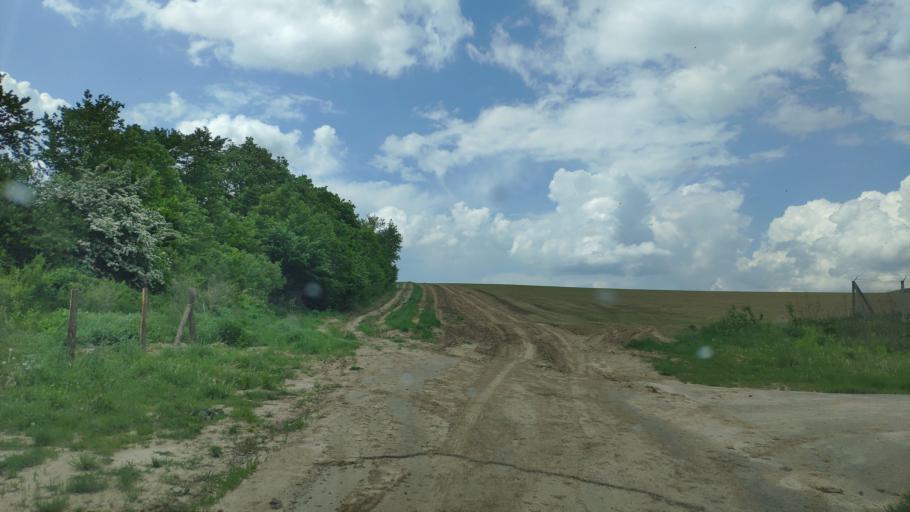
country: SK
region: Presovsky
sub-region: Okres Presov
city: Presov
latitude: 49.0254
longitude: 21.1757
